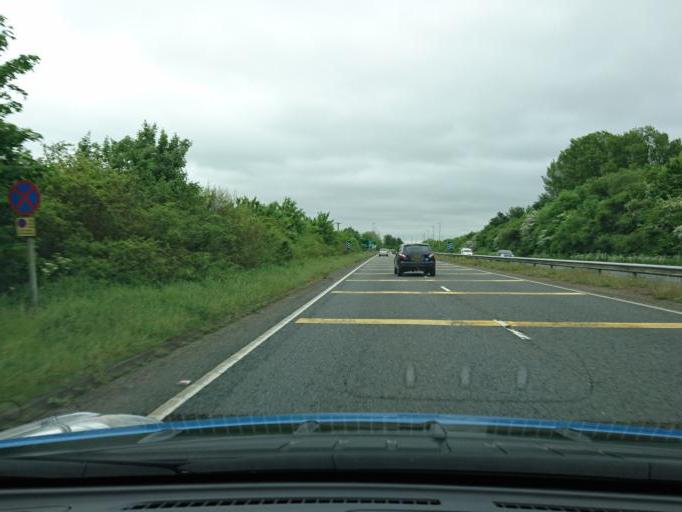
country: GB
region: England
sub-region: Oxfordshire
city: Frilford
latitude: 51.6845
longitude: -1.4183
